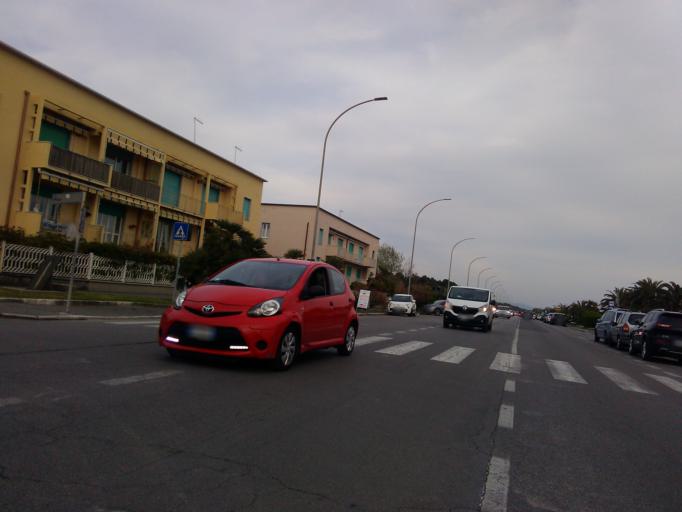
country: IT
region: Tuscany
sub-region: Provincia di Massa-Carrara
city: Massa
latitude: 44.0017
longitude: 10.1090
